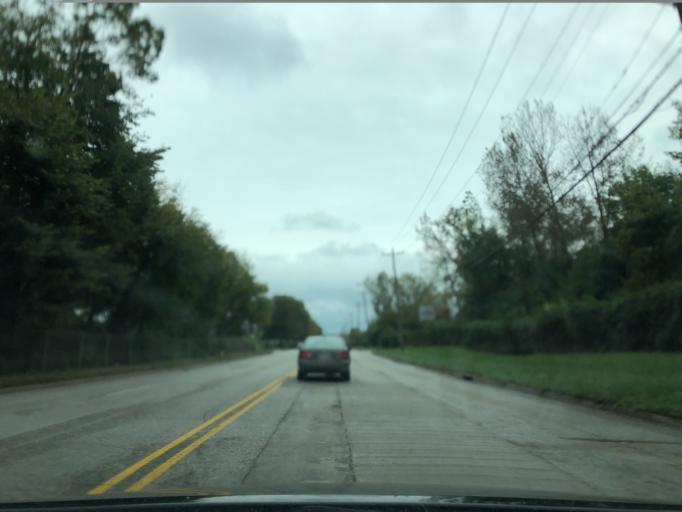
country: US
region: Kentucky
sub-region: Campbell County
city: Fort Thomas
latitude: 39.1066
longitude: -84.4357
